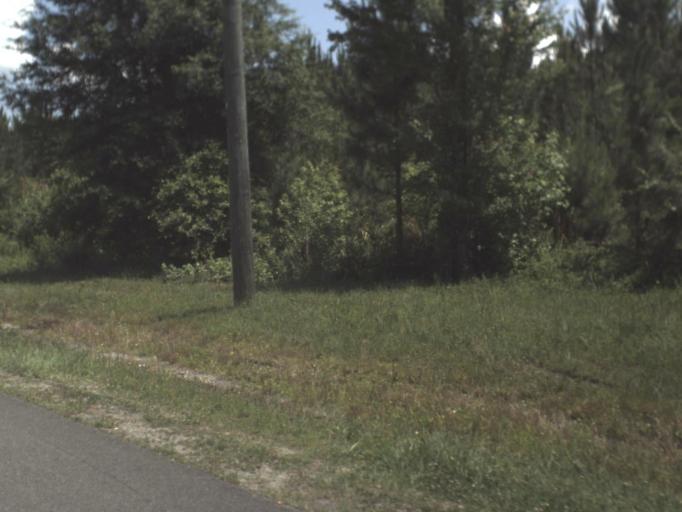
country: US
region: Florida
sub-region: Nassau County
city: Nassau Village-Ratliff
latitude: 30.4734
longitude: -81.7109
